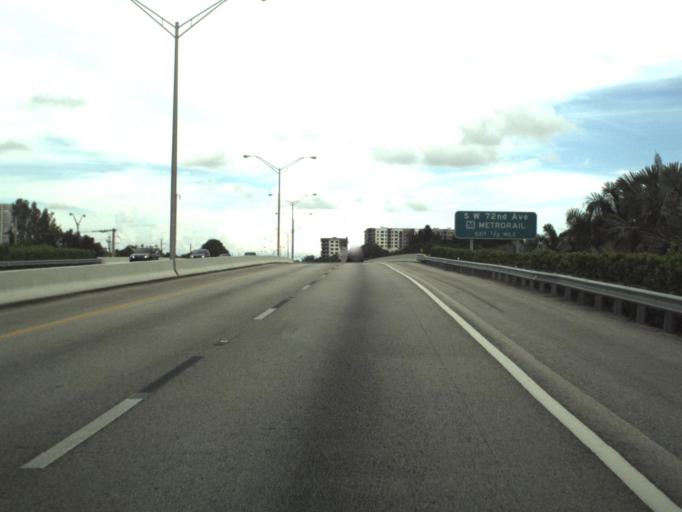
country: US
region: Florida
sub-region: Miami-Dade County
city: Glenvar Heights
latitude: 25.6952
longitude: -80.3187
